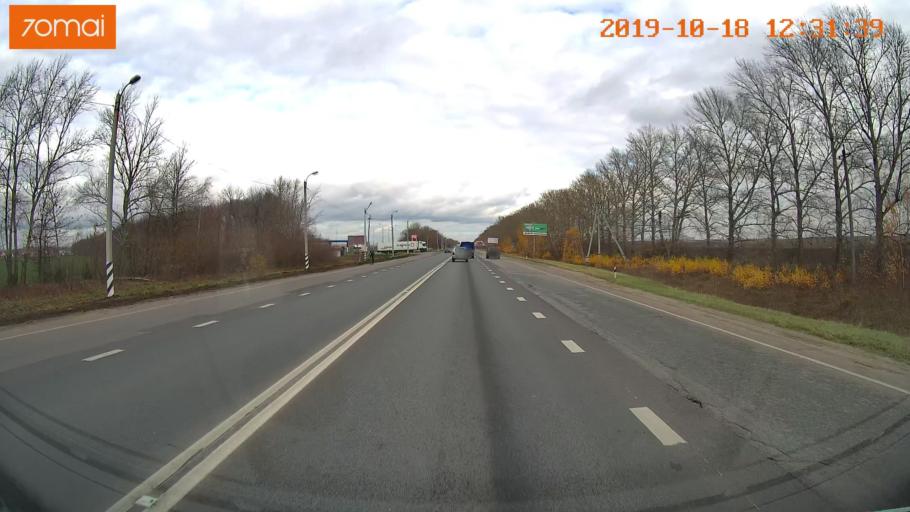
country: RU
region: Rjazan
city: Ryazan'
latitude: 54.5949
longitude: 39.6148
